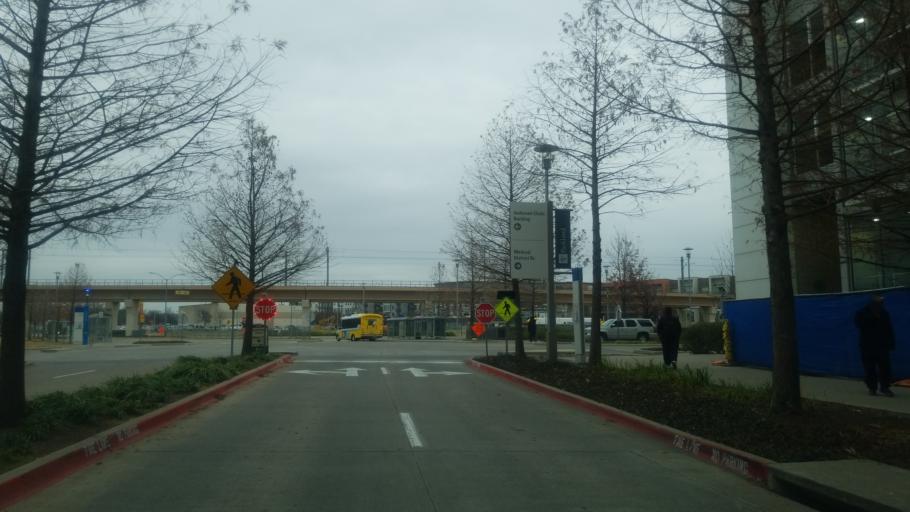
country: US
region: Texas
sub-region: Dallas County
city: Dallas
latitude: 32.8123
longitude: -96.8344
